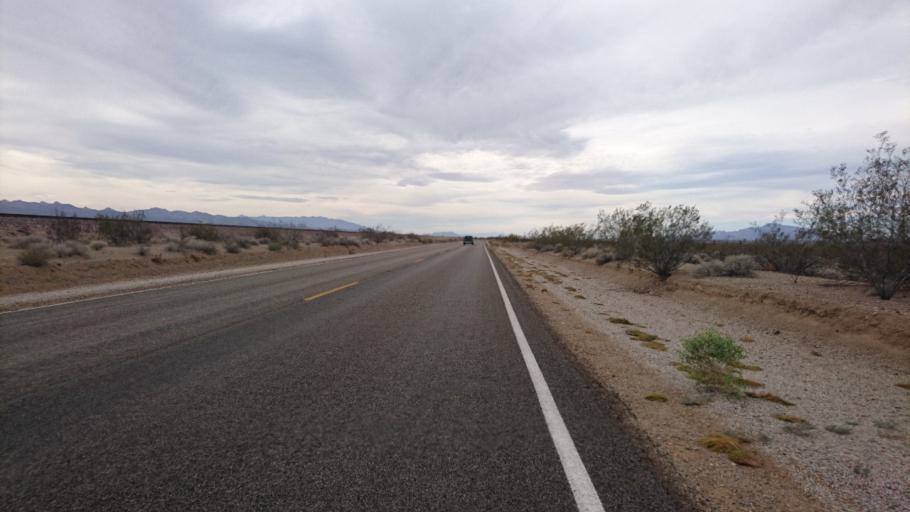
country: US
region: California
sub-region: San Bernardino County
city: Needles
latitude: 34.8771
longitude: -115.1078
